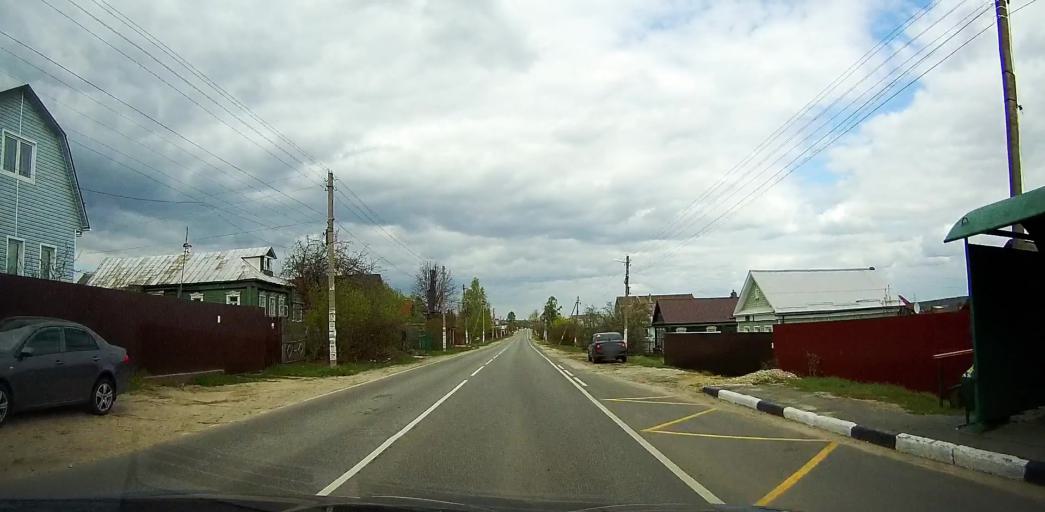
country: RU
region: Moskovskaya
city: Ashitkovo
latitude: 55.4542
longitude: 38.5950
